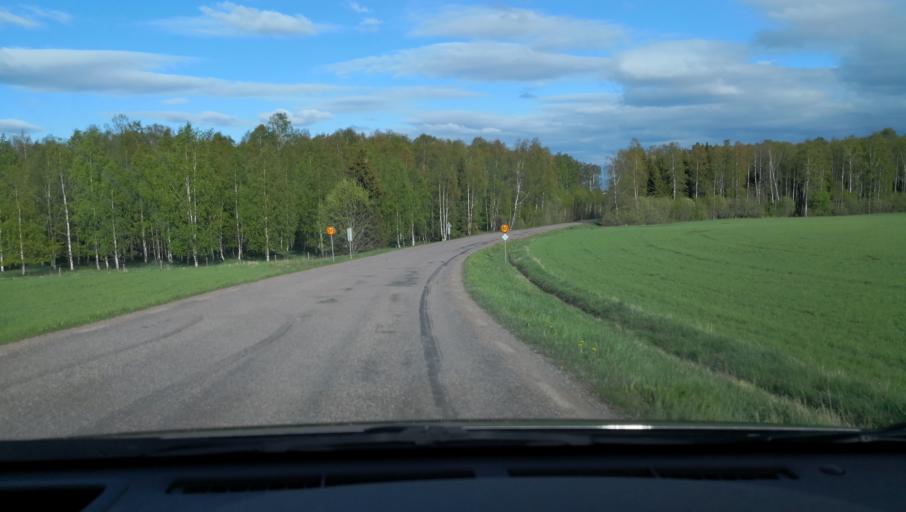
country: SE
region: Dalarna
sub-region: Saters Kommun
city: Saeter
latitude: 60.2994
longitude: 15.8514
